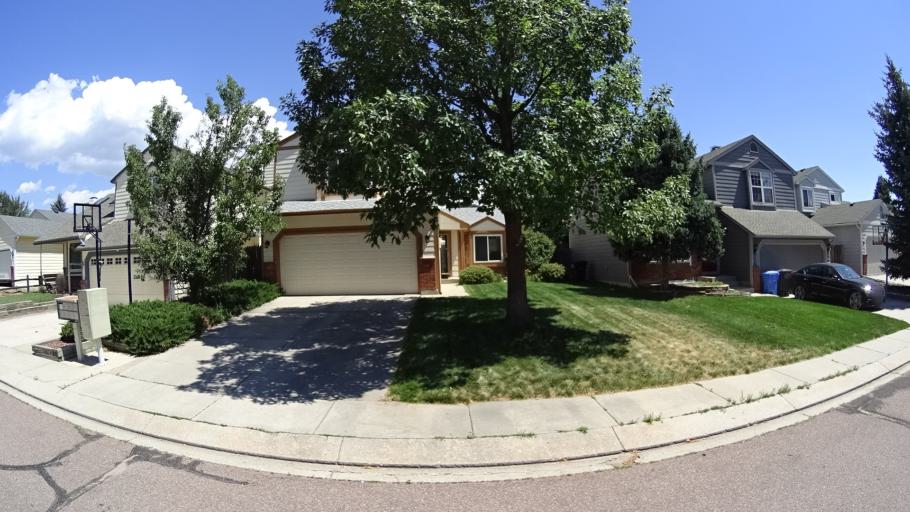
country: US
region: Colorado
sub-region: El Paso County
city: Black Forest
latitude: 38.9530
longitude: -104.7497
